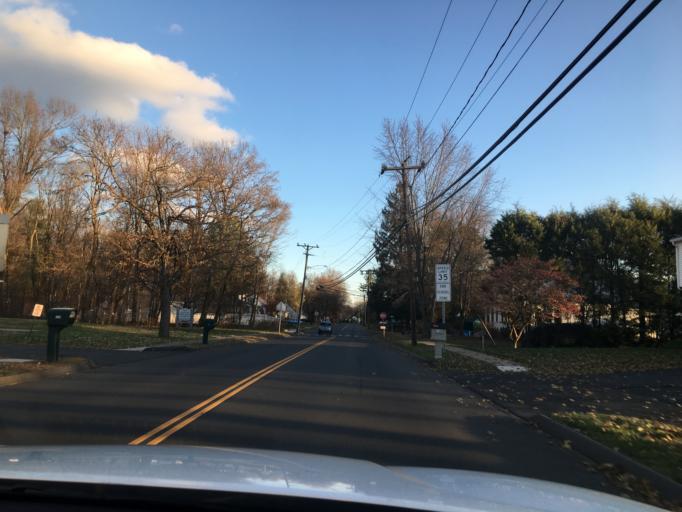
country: US
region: Connecticut
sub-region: Hartford County
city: Southwood Acres
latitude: 41.9604
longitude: -72.5753
